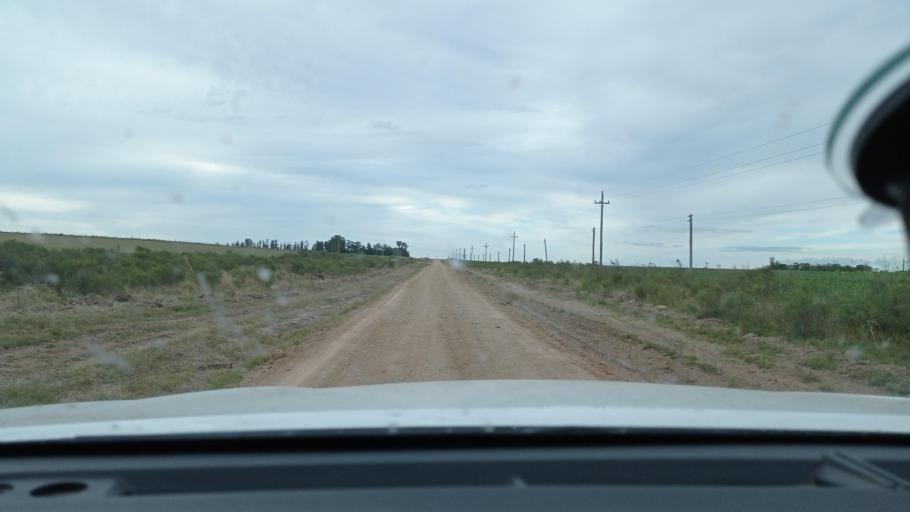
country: UY
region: Florida
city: Casupa
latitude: -34.1176
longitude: -55.7693
